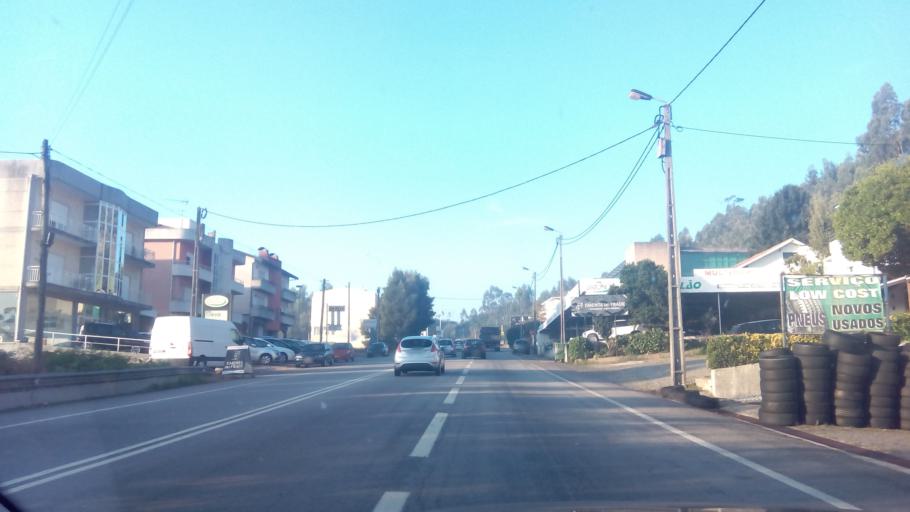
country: PT
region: Porto
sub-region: Paredes
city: Baltar
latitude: 41.1925
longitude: -8.3658
